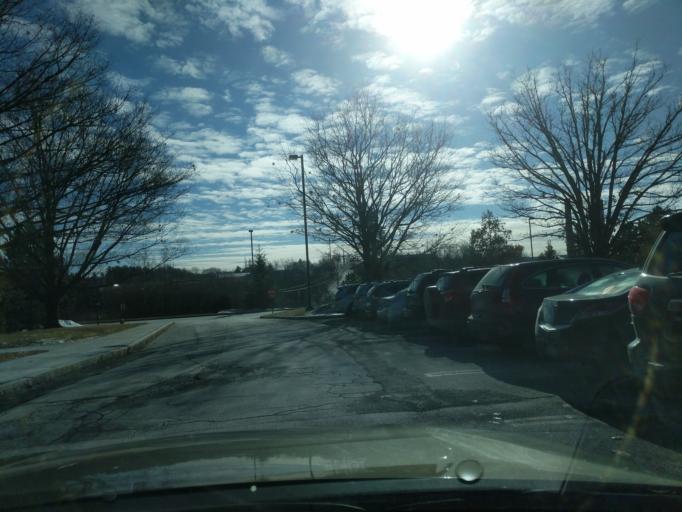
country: US
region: New York
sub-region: Tompkins County
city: East Ithaca
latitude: 42.4461
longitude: -76.4720
